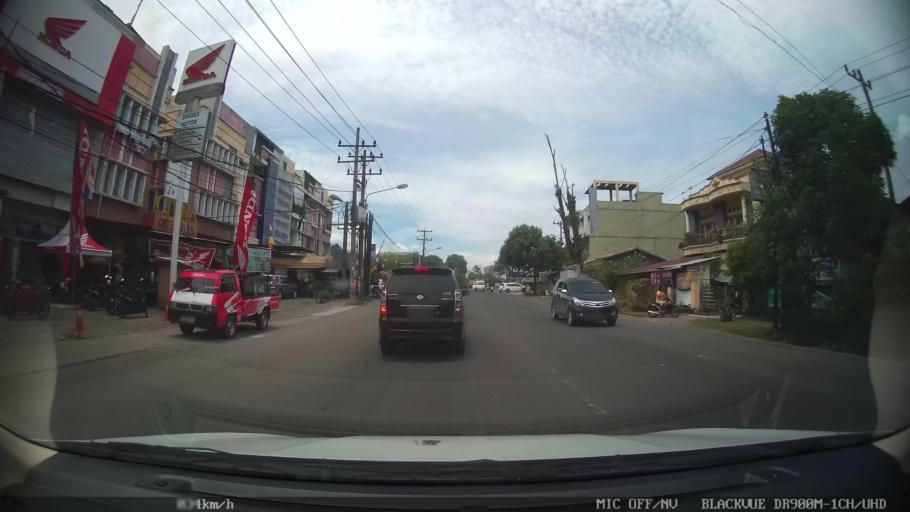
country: ID
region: North Sumatra
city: Sunggal
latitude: 3.5241
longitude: 98.6198
